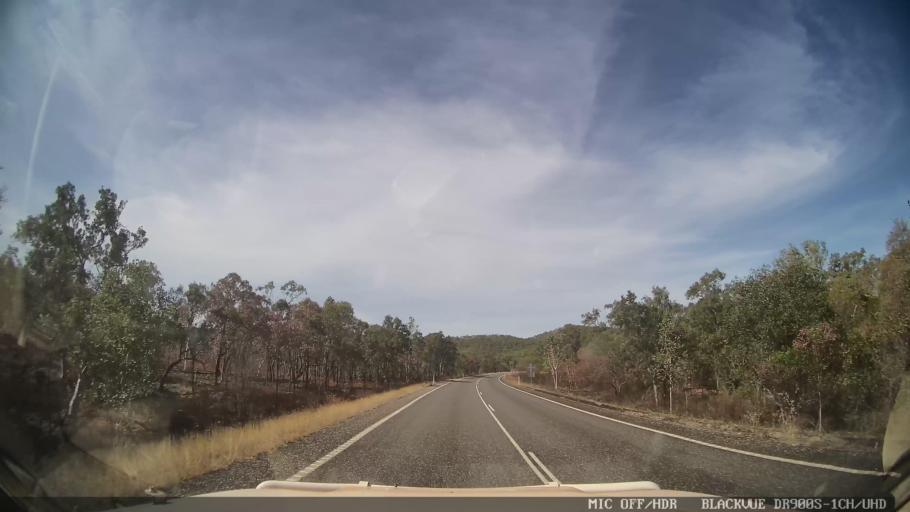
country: AU
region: Queensland
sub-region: Cook
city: Cooktown
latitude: -15.6756
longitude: 145.1782
